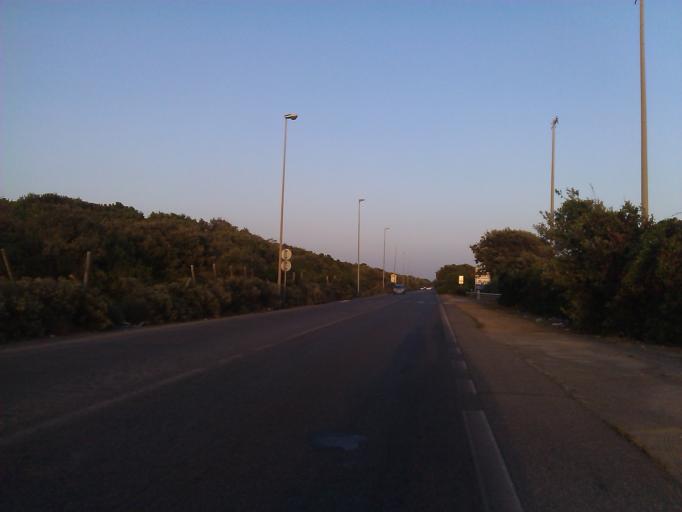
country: IT
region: Latium
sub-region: Citta metropolitana di Roma Capitale
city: Acilia-Castel Fusano-Ostia Antica
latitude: 41.7115
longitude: 12.3268
